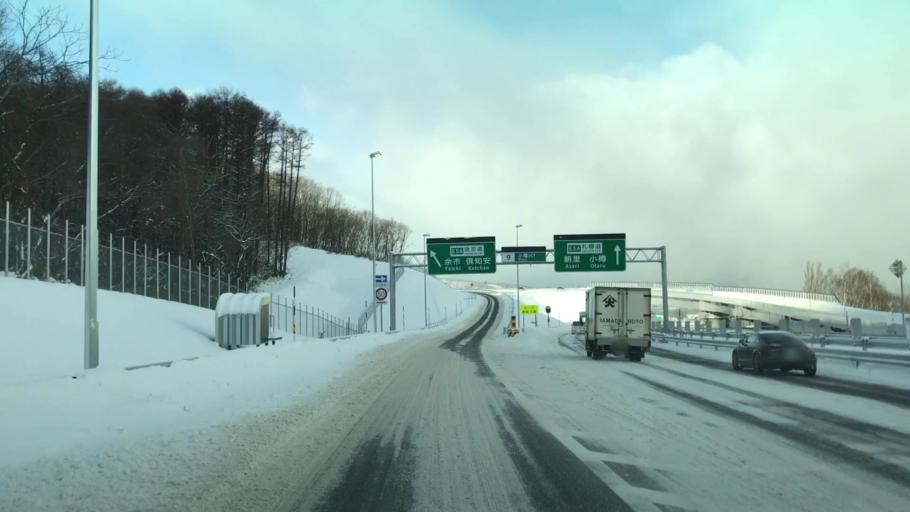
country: JP
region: Hokkaido
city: Otaru
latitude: 43.1694
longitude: 141.0732
